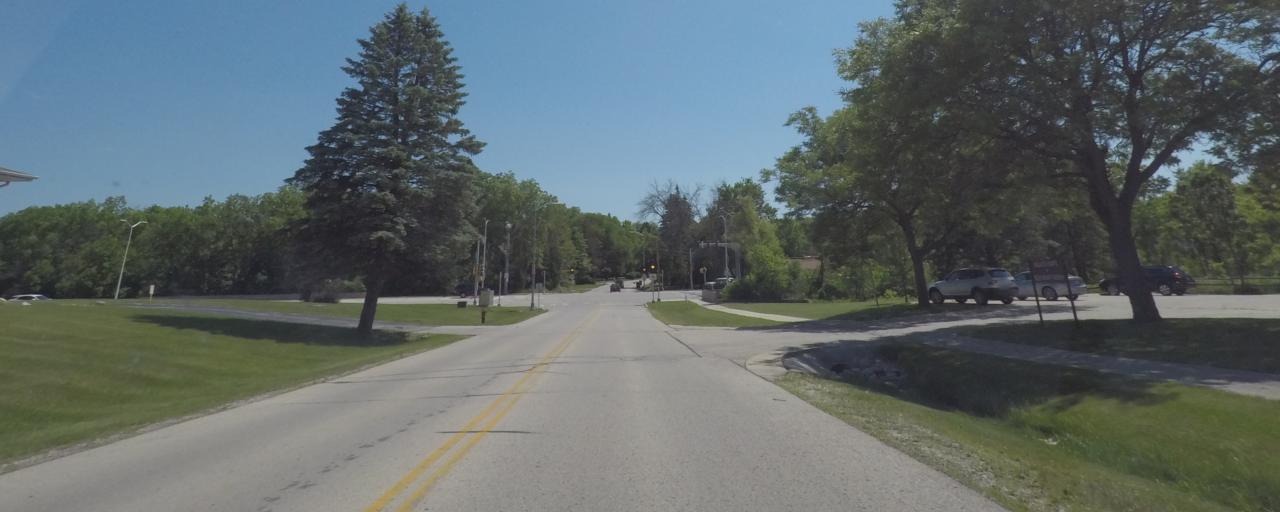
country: US
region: Wisconsin
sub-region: Milwaukee County
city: Hales Corners
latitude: 42.9381
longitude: -88.0584
